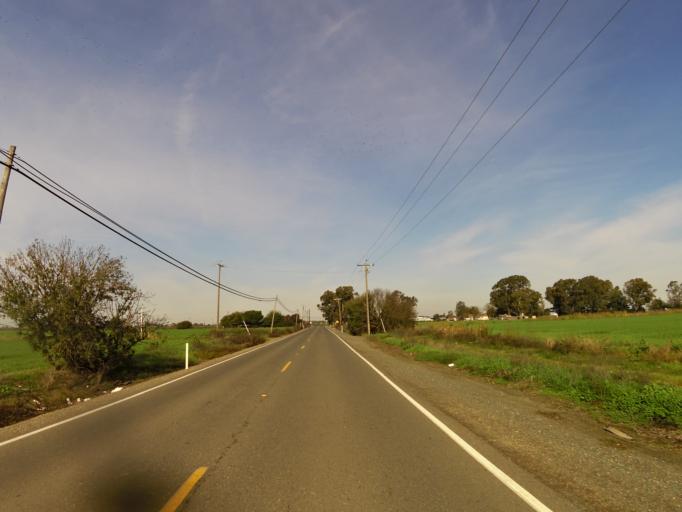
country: US
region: California
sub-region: San Joaquin County
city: Thornton
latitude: 38.3179
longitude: -121.4203
